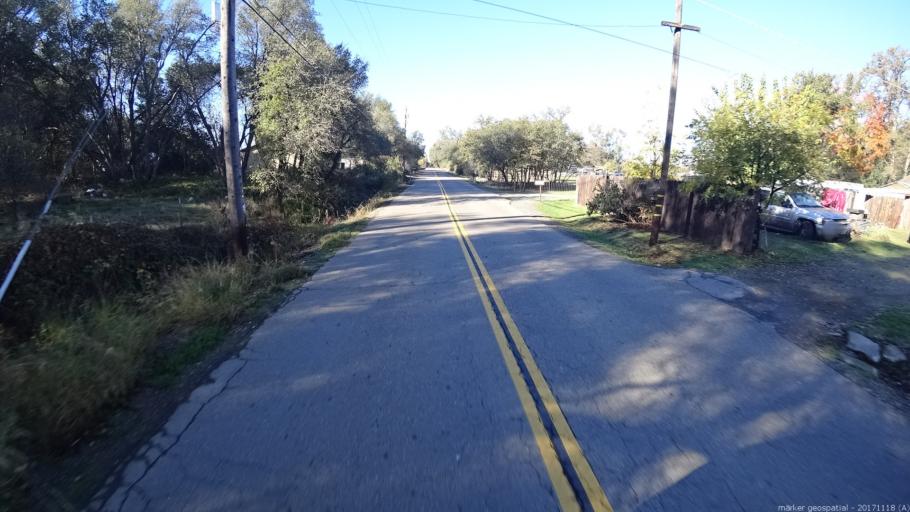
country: US
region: California
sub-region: Shasta County
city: Cottonwood
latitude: 40.3856
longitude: -122.3155
